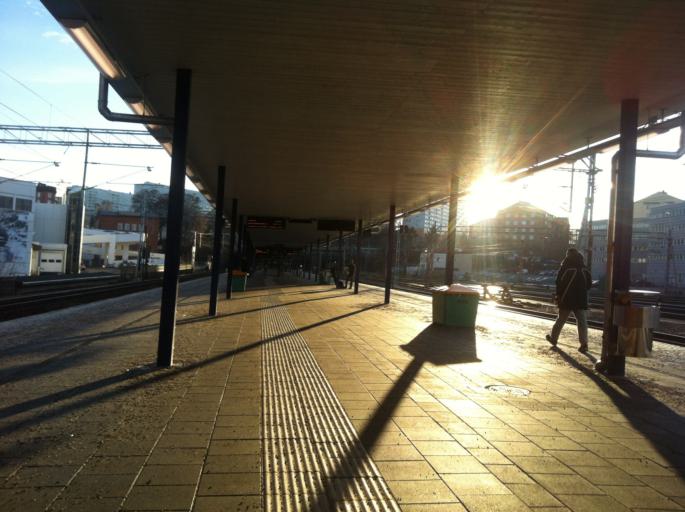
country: SE
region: Stockholm
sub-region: Solna Kommun
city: Solna
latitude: 59.3677
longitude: 18.0093
